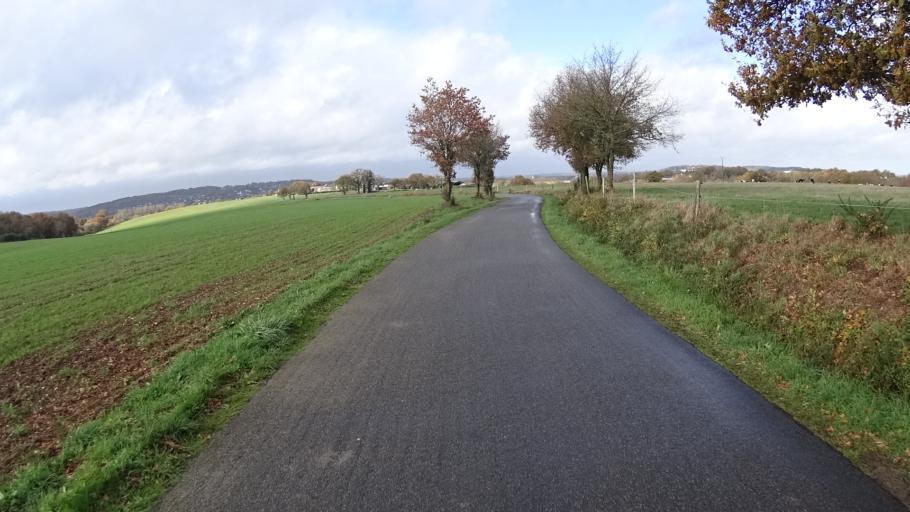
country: FR
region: Pays de la Loire
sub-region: Departement de la Loire-Atlantique
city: Saint-Nicolas-de-Redon
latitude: 47.6223
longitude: -2.0664
